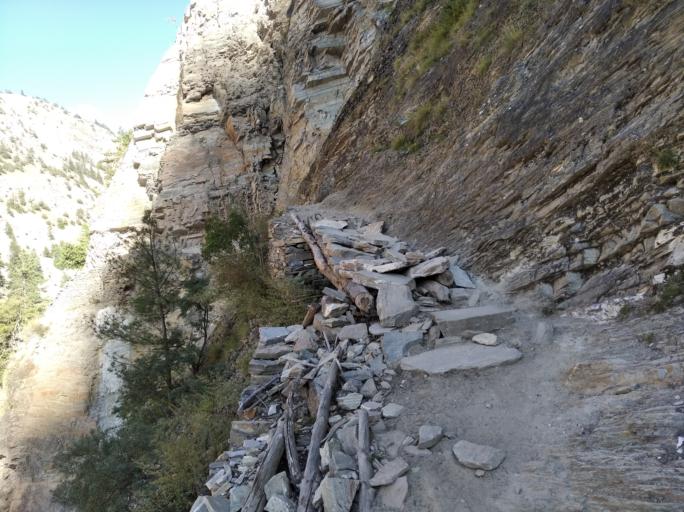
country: NP
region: Western Region
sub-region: Dhawalagiri Zone
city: Jomsom
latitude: 28.8743
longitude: 83.1366
